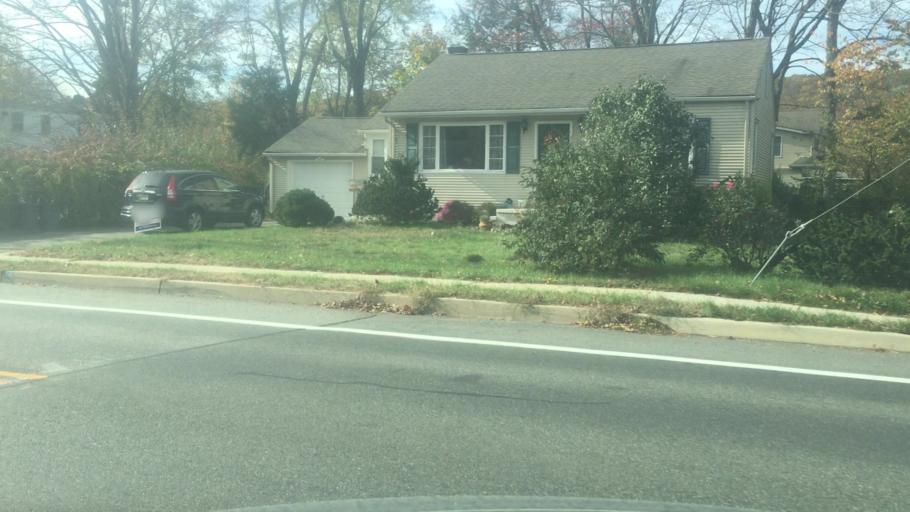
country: US
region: New Jersey
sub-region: Morris County
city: Butler
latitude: 41.0180
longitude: -74.3355
